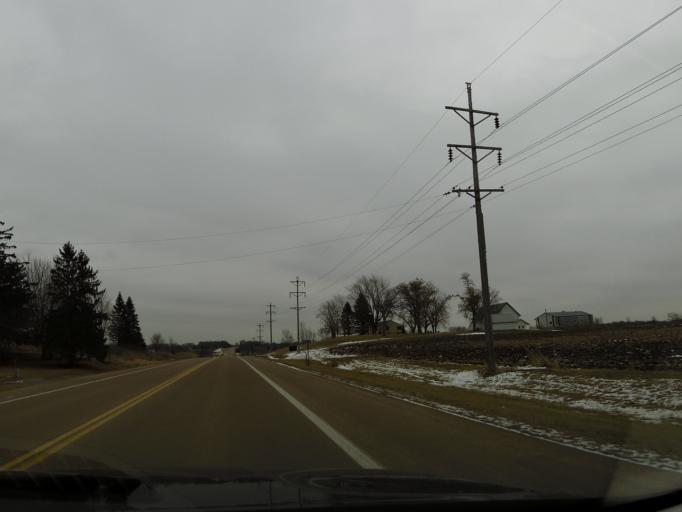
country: US
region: Minnesota
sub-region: Carver County
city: Watertown
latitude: 44.9632
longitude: -93.8178
